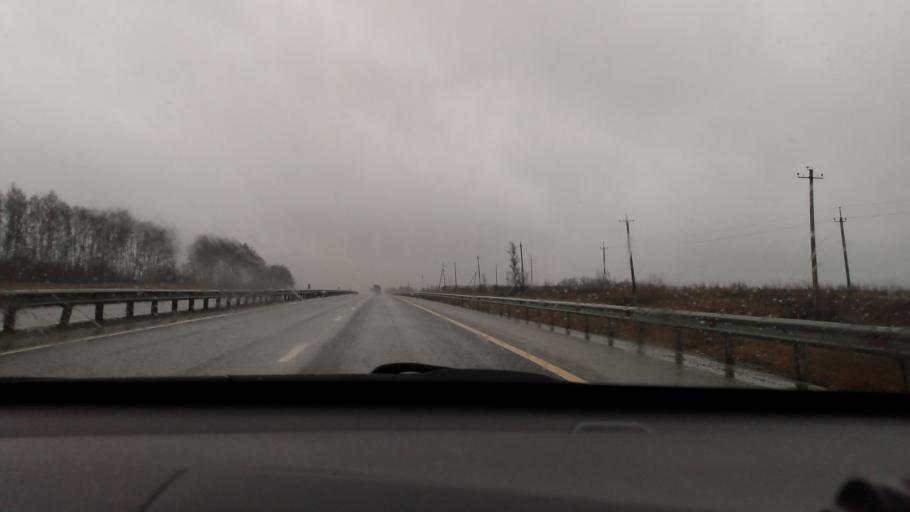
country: RU
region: Tula
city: Venev
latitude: 54.3118
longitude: 38.1547
